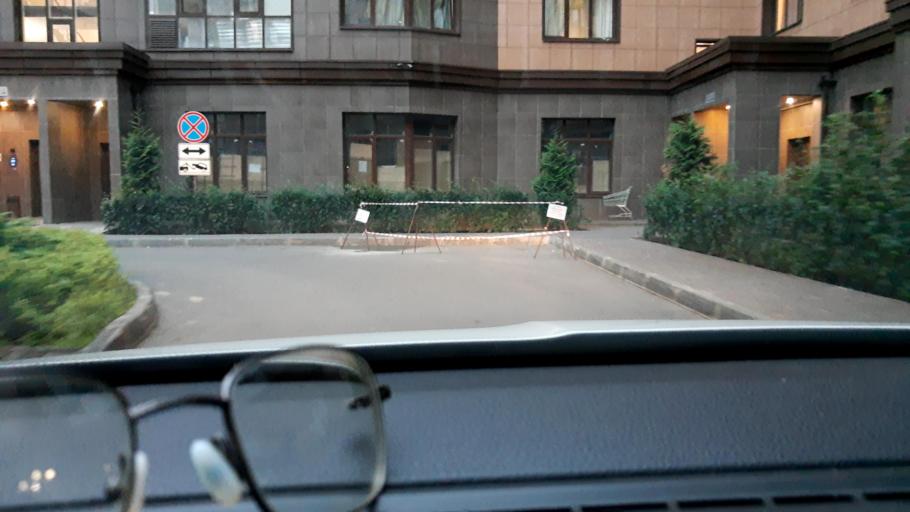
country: RU
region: Moskovskaya
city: Kommunarka
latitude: 55.5687
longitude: 37.4405
